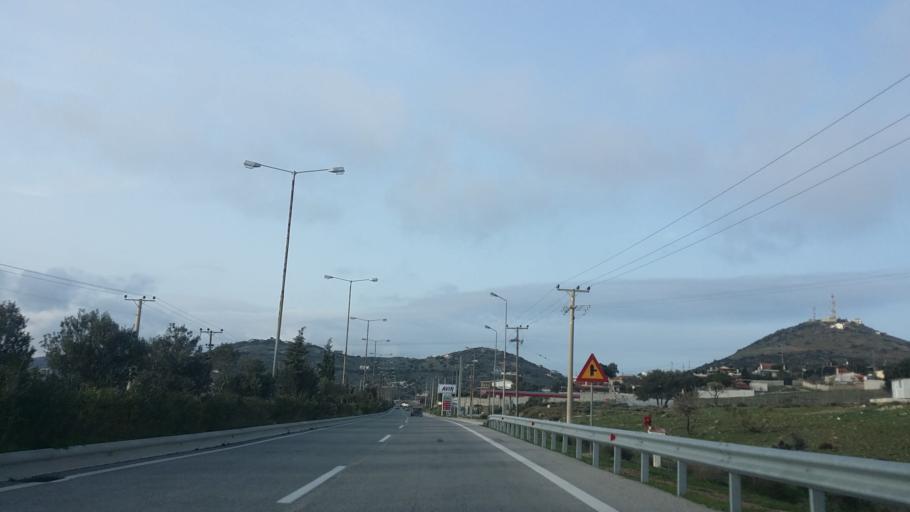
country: GR
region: Attica
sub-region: Nomarchia Anatolikis Attikis
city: Lavrio
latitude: 37.7846
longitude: 24.0575
